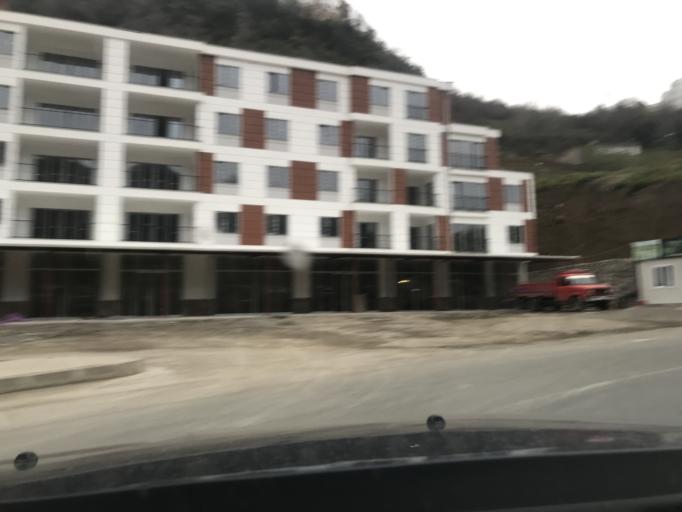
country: TR
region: Trabzon
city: Akcaabat
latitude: 41.0005
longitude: 39.6268
